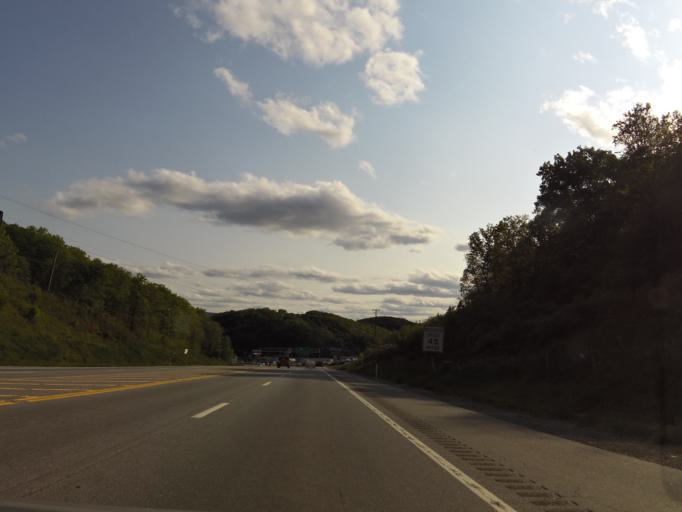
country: US
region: West Virginia
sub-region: Mercer County
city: Princeton
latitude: 37.3268
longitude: -81.1321
